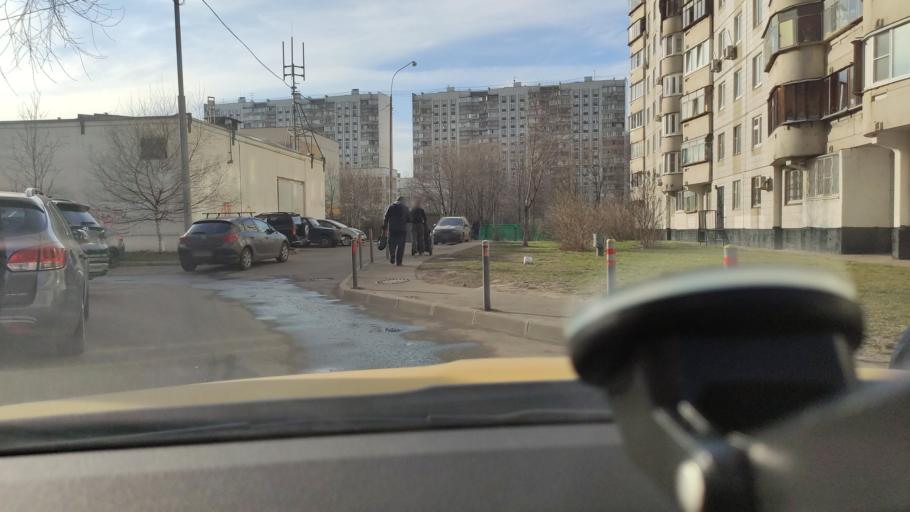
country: RU
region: Moskovskaya
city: Pavshino
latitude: 55.8471
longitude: 37.3676
